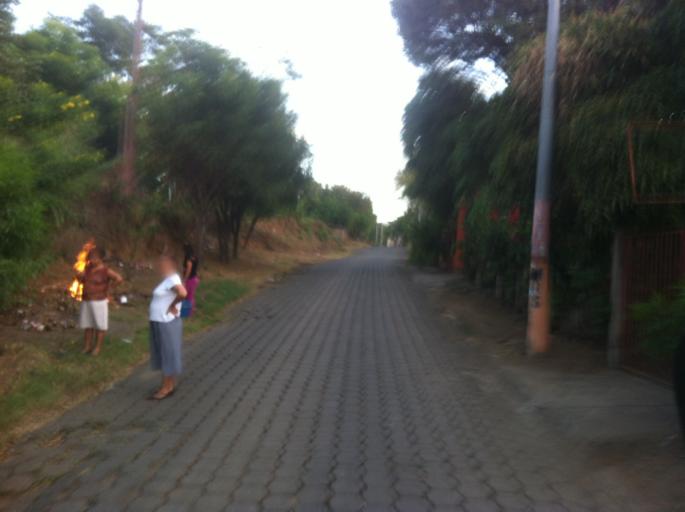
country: NI
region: Managua
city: Ciudad Sandino
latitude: 12.0763
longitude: -86.3309
